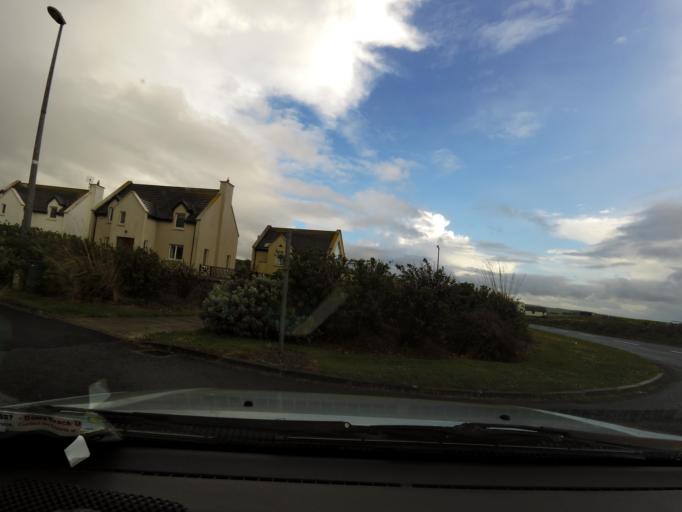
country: IE
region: Munster
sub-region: An Clar
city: Kilrush
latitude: 52.9264
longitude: -9.3473
